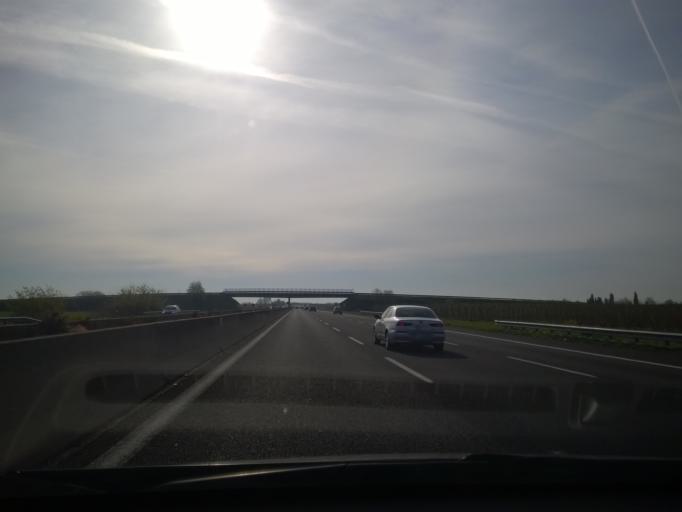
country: IT
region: Emilia-Romagna
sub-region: Provincia di Bologna
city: Bubano
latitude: 44.3738
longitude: 11.7615
